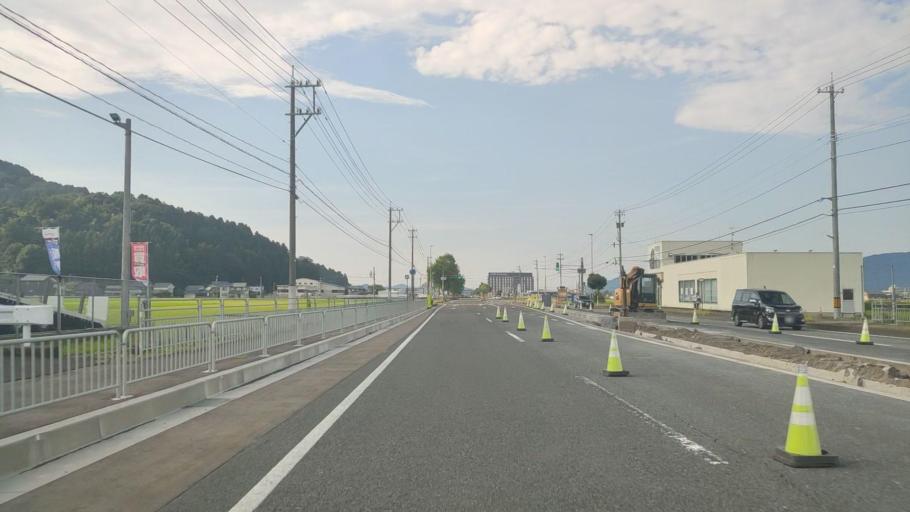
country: JP
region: Fukui
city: Takefu
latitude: 35.8960
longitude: 136.1923
